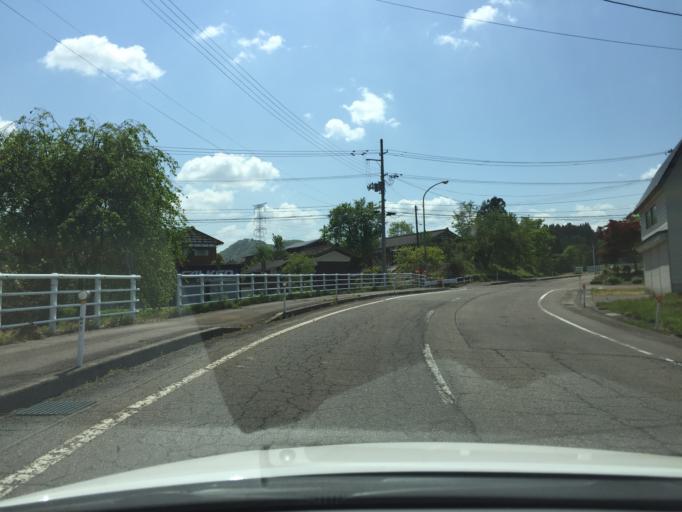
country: JP
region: Niigata
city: Tochio-honcho
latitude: 37.5440
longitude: 139.0927
